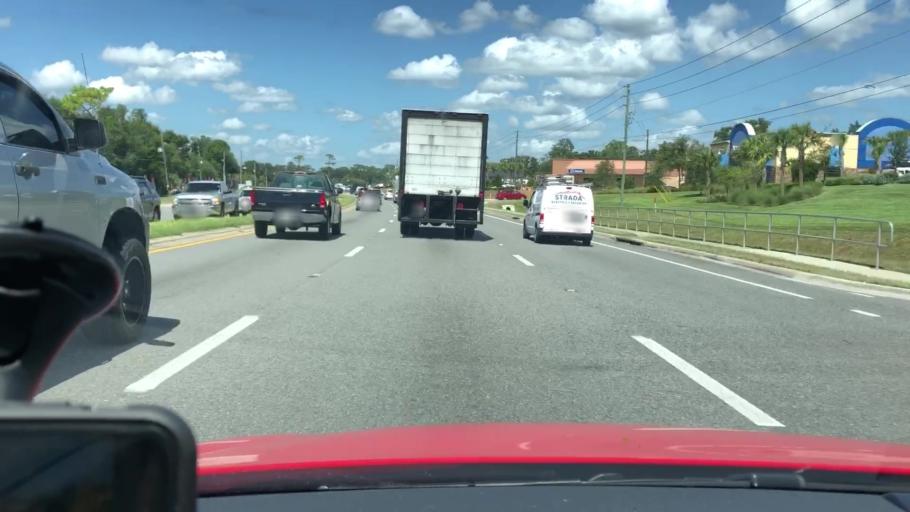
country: US
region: Florida
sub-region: Volusia County
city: De Land Southwest
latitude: 28.9873
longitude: -81.2999
